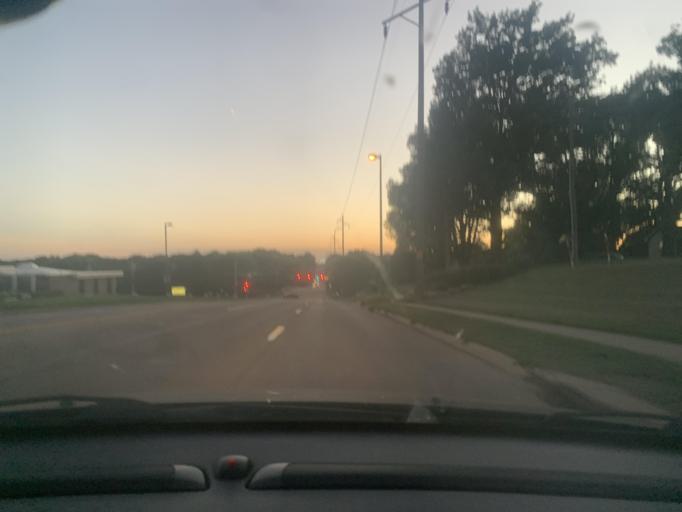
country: US
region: Nebraska
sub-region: Douglas County
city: Ralston
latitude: 41.2778
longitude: -96.0605
